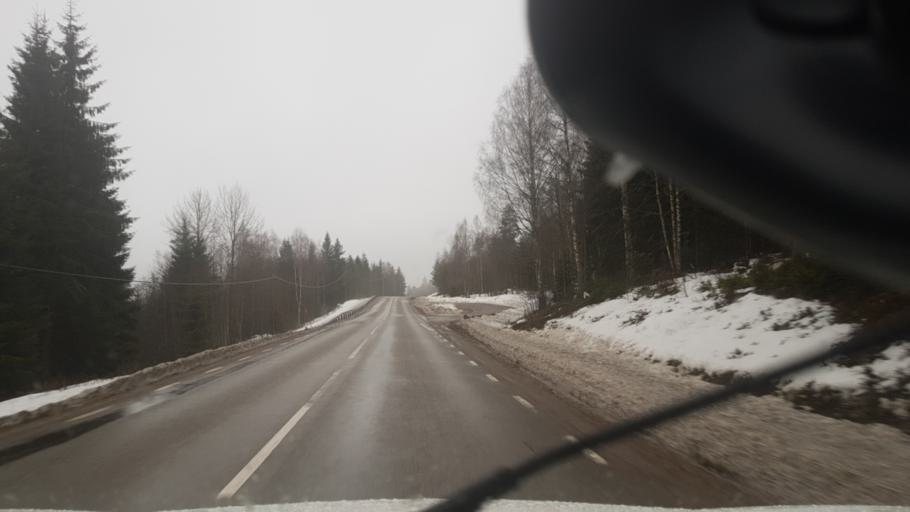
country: SE
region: Vaermland
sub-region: Arjangs Kommun
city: Arjaeng
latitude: 59.5609
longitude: 12.1739
